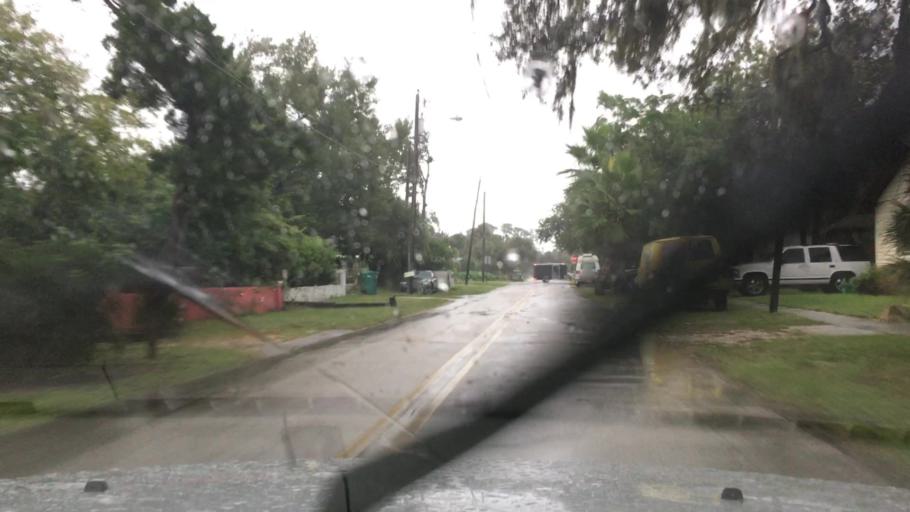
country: US
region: Florida
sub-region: Volusia County
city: Holly Hill
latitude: 29.2511
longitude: -81.0413
